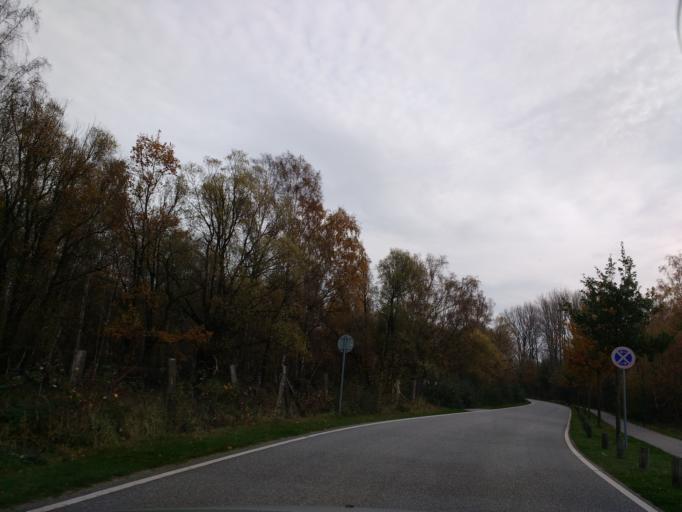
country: DE
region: Mecklenburg-Vorpommern
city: Ostseebad Boltenhagen
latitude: 53.9794
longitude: 11.2439
